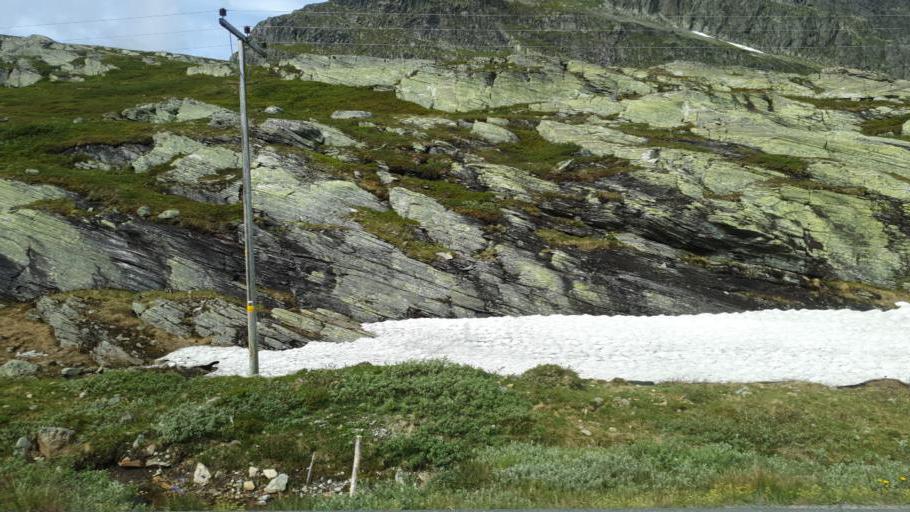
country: NO
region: Oppland
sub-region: Vestre Slidre
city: Slidre
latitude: 61.2928
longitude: 8.8136
